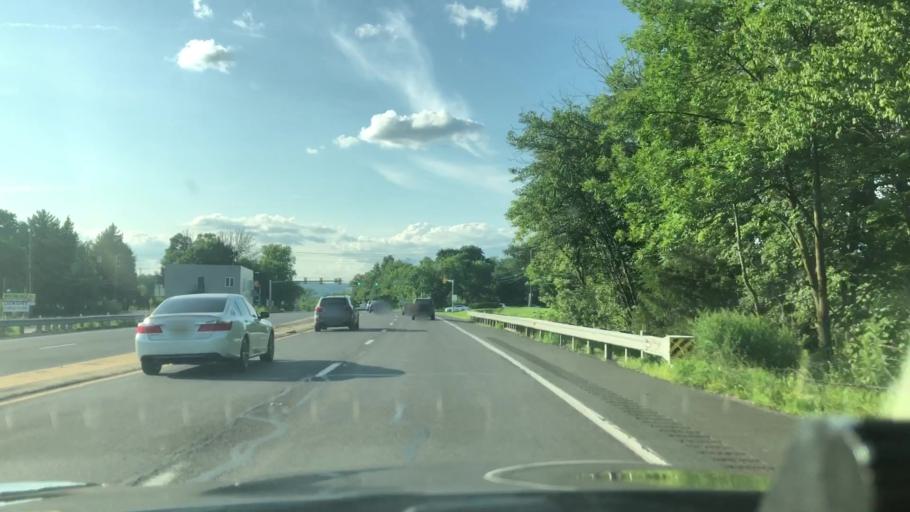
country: US
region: Pennsylvania
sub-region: Lehigh County
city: Coopersburg
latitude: 40.5219
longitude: -75.3871
